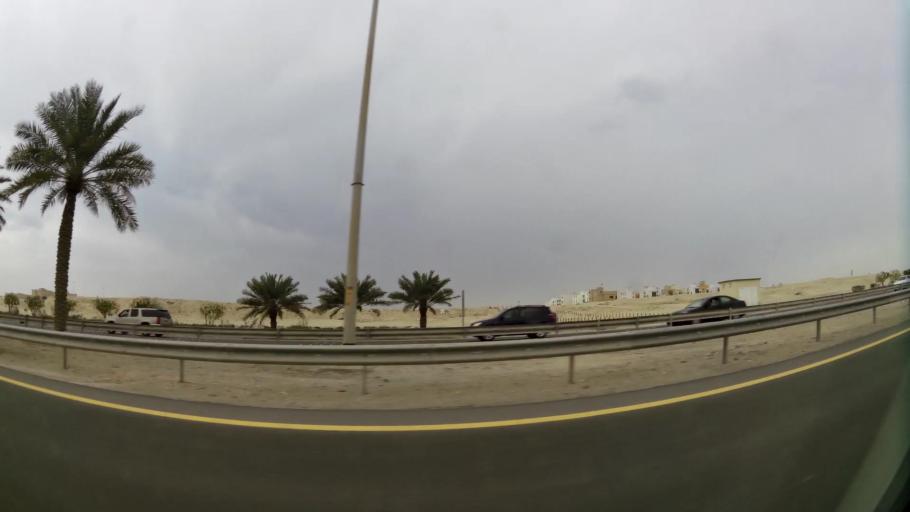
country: BH
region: Central Governorate
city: Dar Kulayb
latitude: 26.0880
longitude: 50.5154
